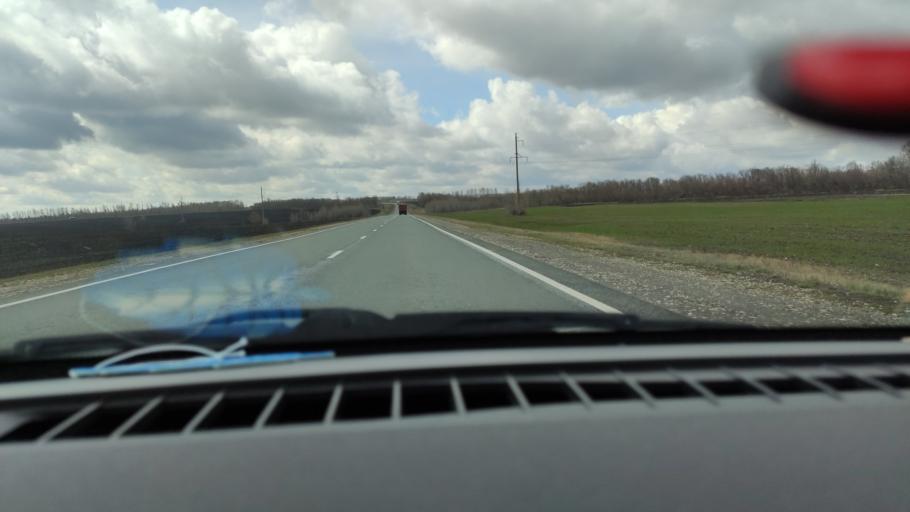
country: RU
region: Samara
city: Yelkhovka
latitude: 53.8809
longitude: 50.2600
